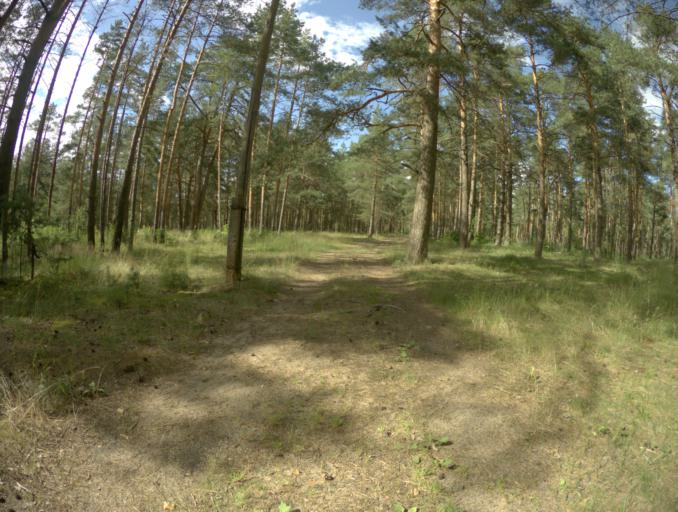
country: RU
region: Vladimir
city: Kommunar
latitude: 56.0948
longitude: 40.4390
